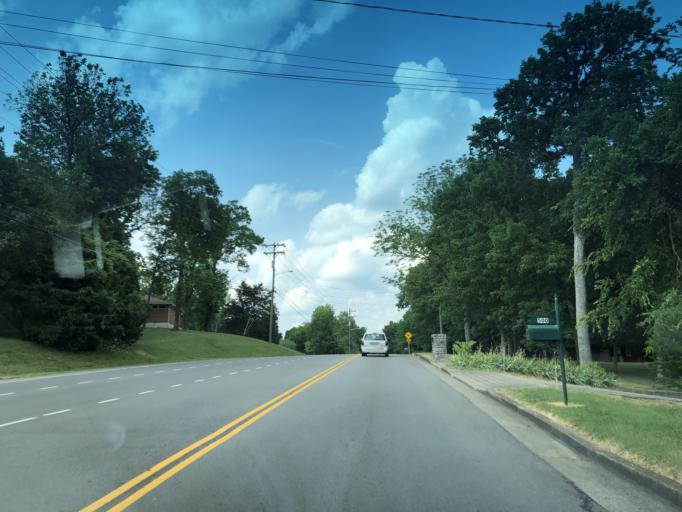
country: US
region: Tennessee
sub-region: Davidson County
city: Goodlettsville
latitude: 36.2657
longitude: -86.7319
